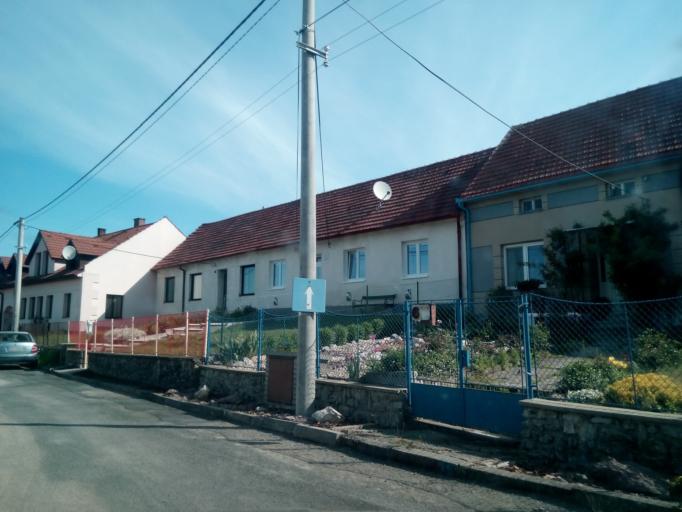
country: CZ
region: South Moravian
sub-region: Okres Blansko
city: Jedovnice
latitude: 49.3627
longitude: 16.7476
